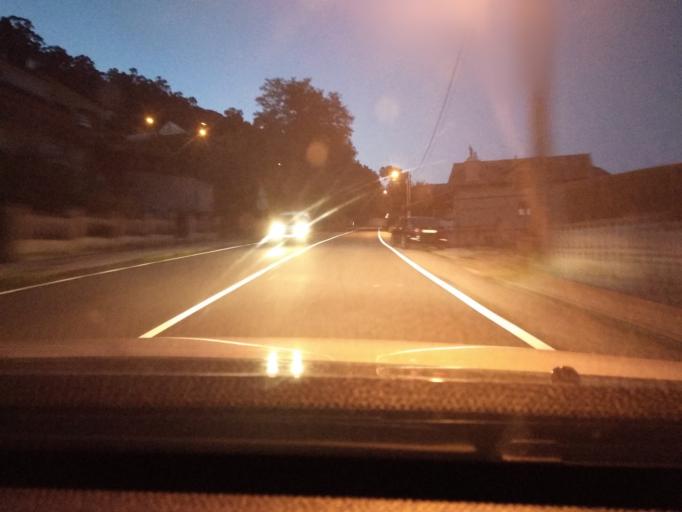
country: ES
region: Galicia
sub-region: Provincia de Pontevedra
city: Moana
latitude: 42.2939
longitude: -8.7420
